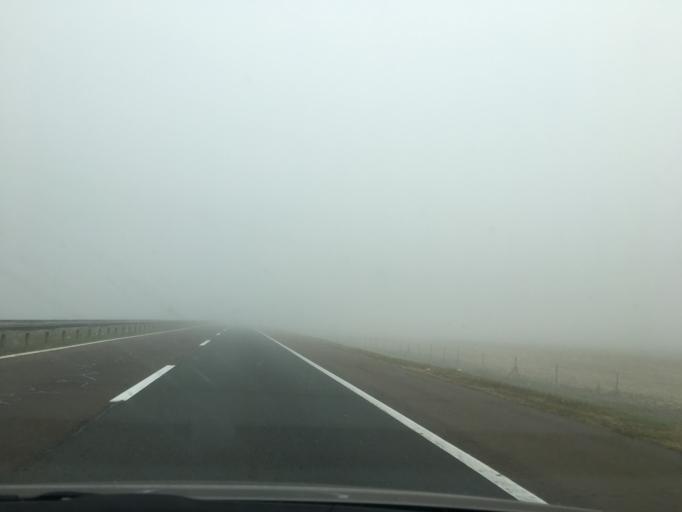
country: RS
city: Novi Karlovci
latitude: 45.0301
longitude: 20.1882
